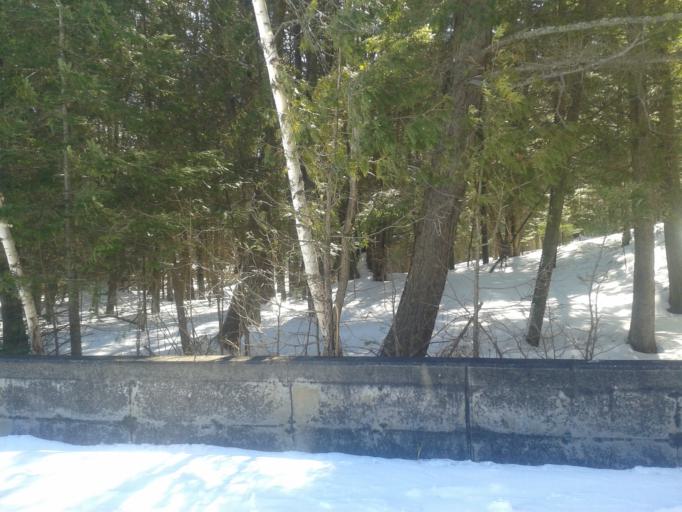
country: CA
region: Ontario
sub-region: Nipissing District
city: North Bay
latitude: 46.3432
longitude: -79.4955
